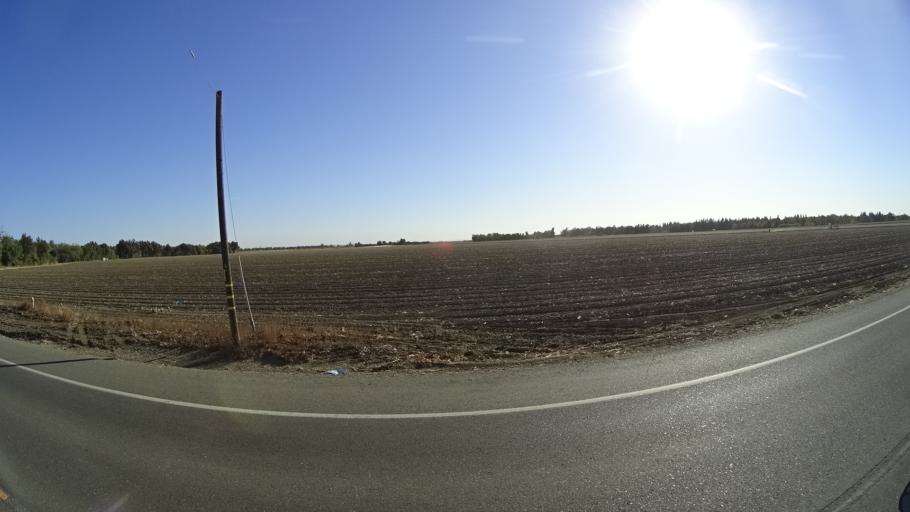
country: US
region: California
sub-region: Yolo County
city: Davis
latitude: 38.5941
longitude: -121.7856
